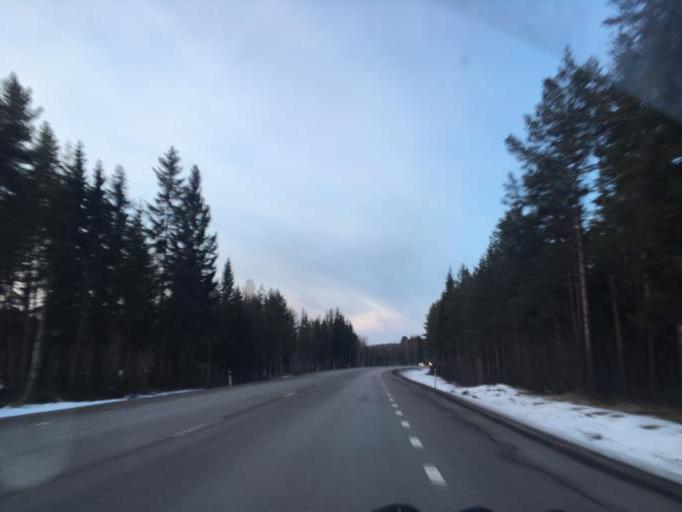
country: SE
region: Dalarna
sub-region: Leksand Municipality
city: Leksand
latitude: 60.7710
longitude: 15.0186
